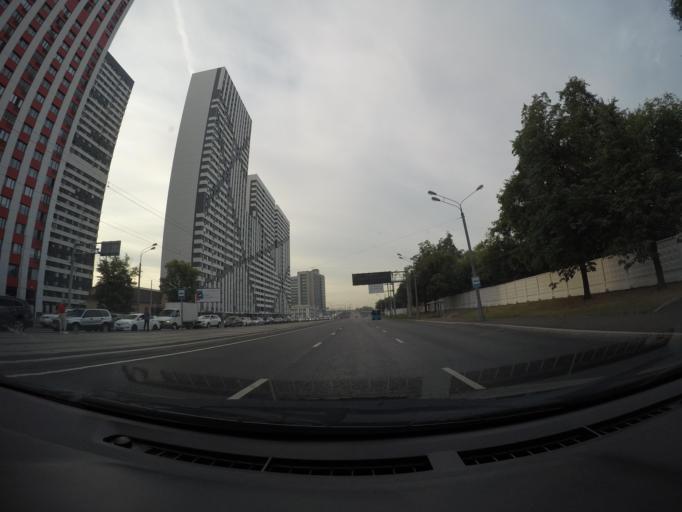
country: RU
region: Moscow
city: Lefortovo
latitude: 55.7604
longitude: 37.7368
